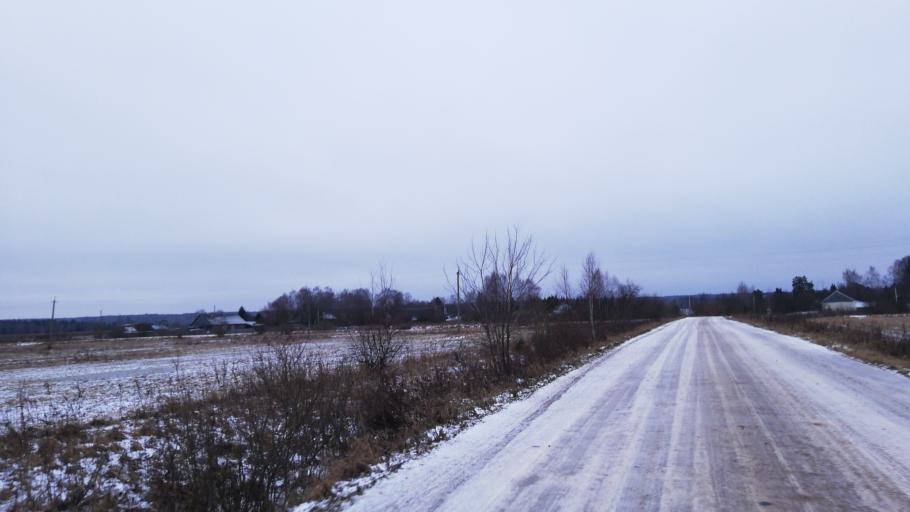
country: RU
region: Kostroma
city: Krasnoye-na-Volge
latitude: 57.6743
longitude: 41.1947
